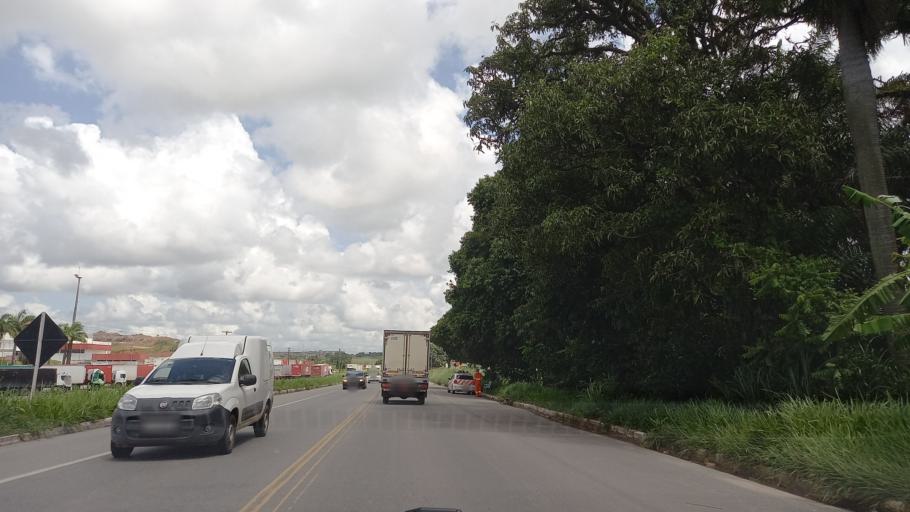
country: BR
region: Pernambuco
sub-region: Cabo De Santo Agostinho
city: Cabo
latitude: -8.2469
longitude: -34.9976
